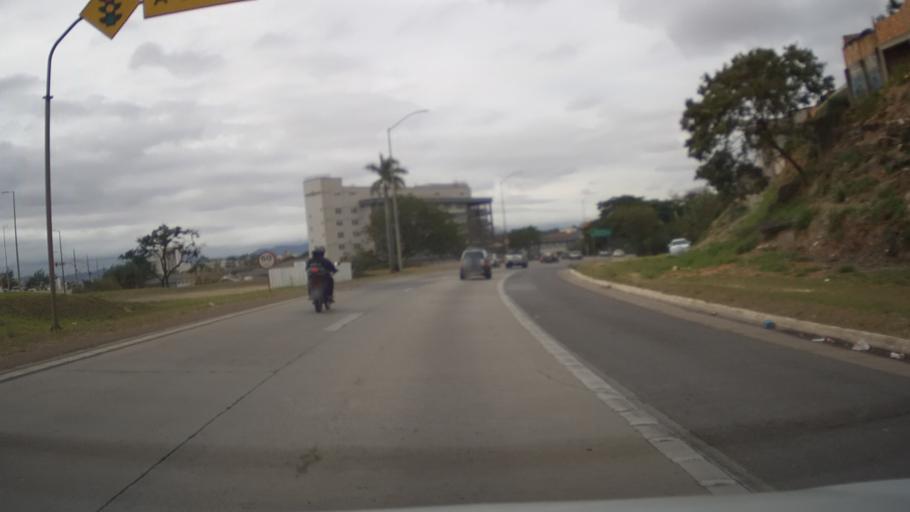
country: BR
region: Minas Gerais
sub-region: Belo Horizonte
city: Belo Horizonte
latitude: -19.8155
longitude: -43.9492
